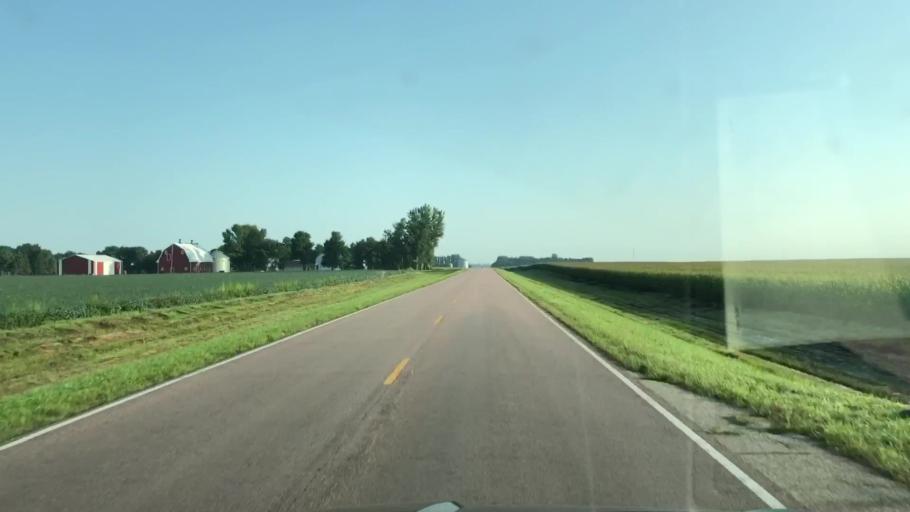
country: US
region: Iowa
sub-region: Lyon County
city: George
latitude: 43.3091
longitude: -95.9991
